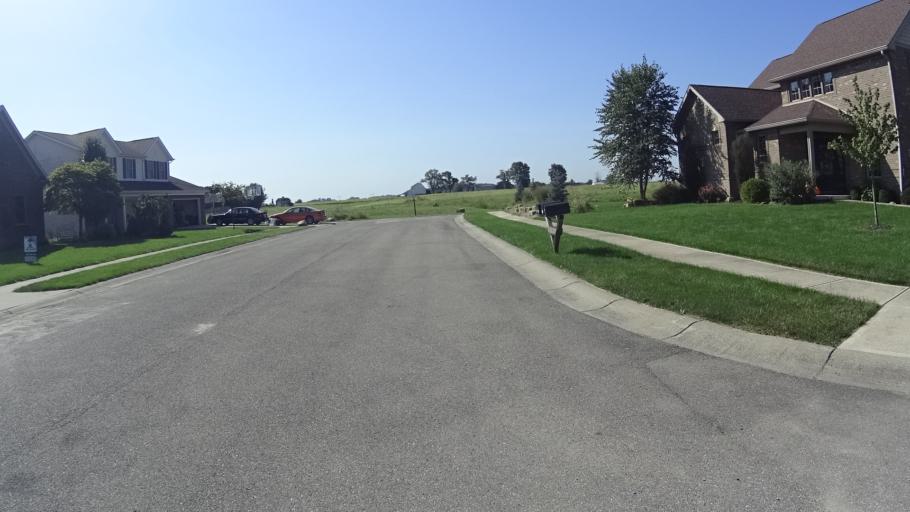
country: US
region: Indiana
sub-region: Madison County
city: Lapel
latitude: 40.0585
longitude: -85.8504
